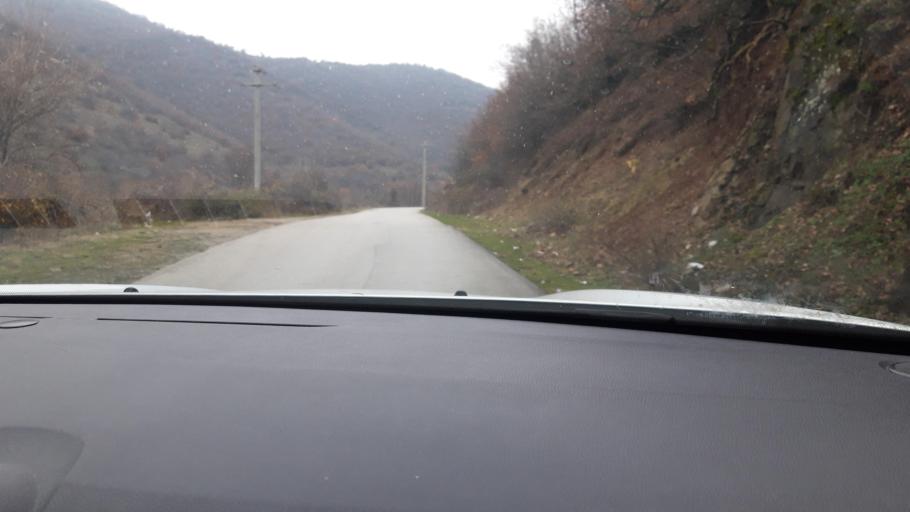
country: MK
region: Opstina Lipkovo
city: Lipkovo
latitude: 42.1736
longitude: 21.5677
